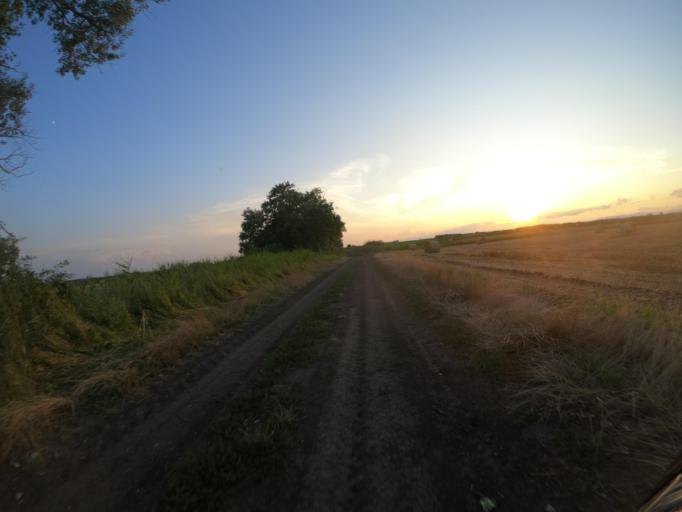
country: HU
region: Borsod-Abauj-Zemplen
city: Szentistvan
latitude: 47.7463
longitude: 20.7407
